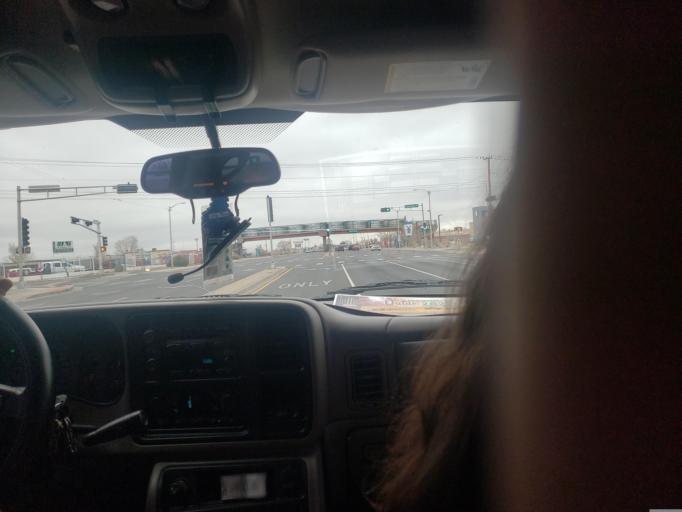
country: US
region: New Mexico
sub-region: Bernalillo County
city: Albuquerque
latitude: 35.0938
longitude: -106.7097
